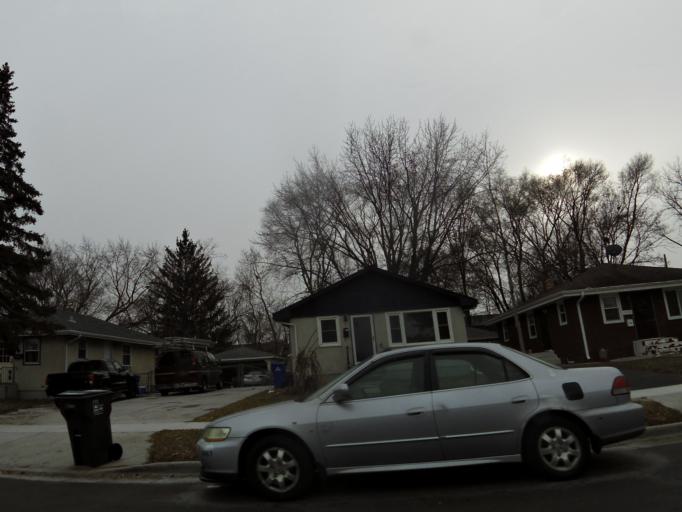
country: US
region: Minnesota
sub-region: Ramsey County
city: Maplewood
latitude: 44.9568
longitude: -93.0344
